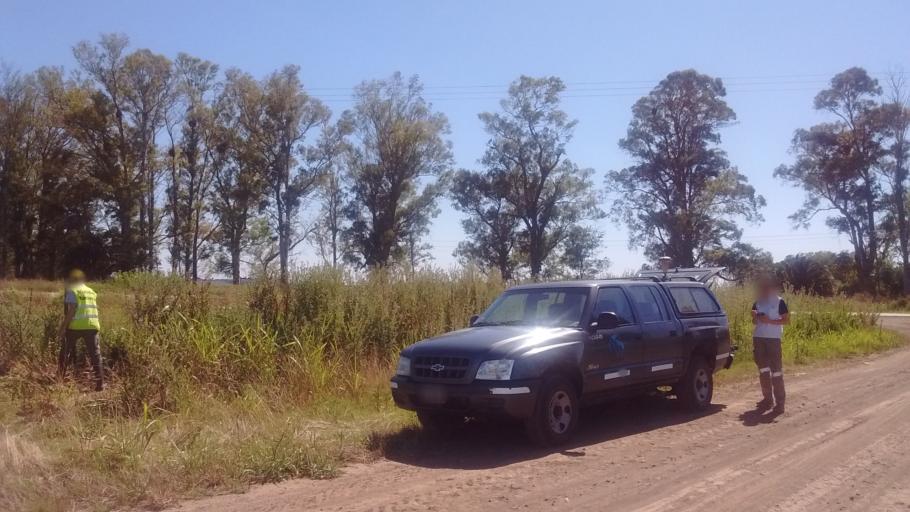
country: AR
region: Santa Fe
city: Las Rosas
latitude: -32.5163
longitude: -61.5545
